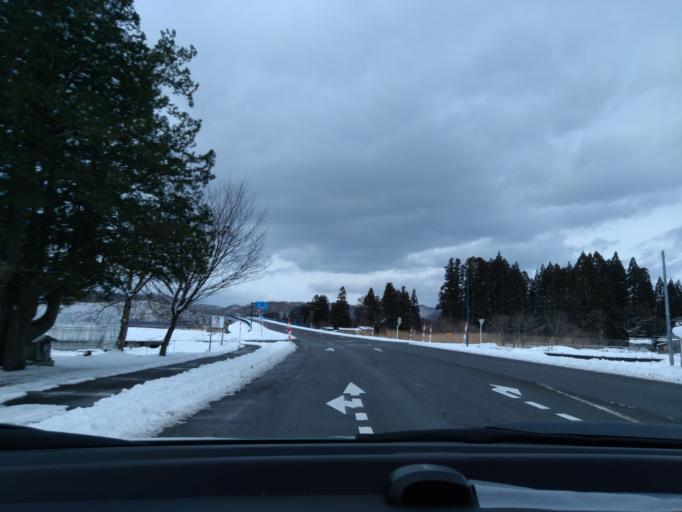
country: JP
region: Akita
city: Kakunodatemachi
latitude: 39.6206
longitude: 140.6313
